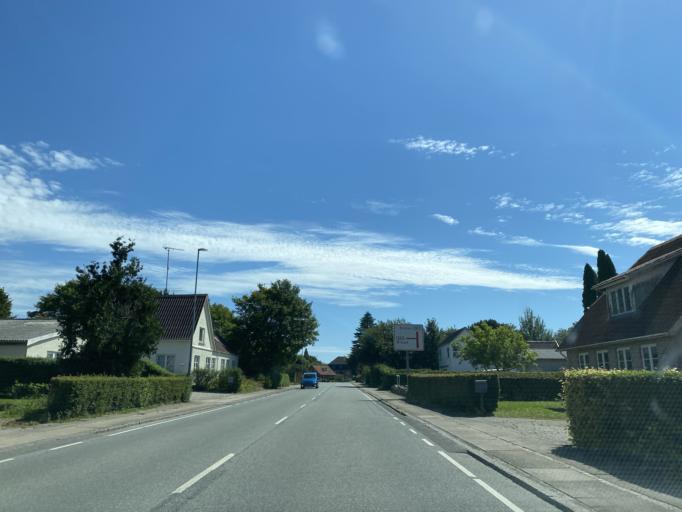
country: DK
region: South Denmark
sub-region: Faaborg-Midtfyn Kommune
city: Ringe
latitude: 55.2372
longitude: 10.5615
